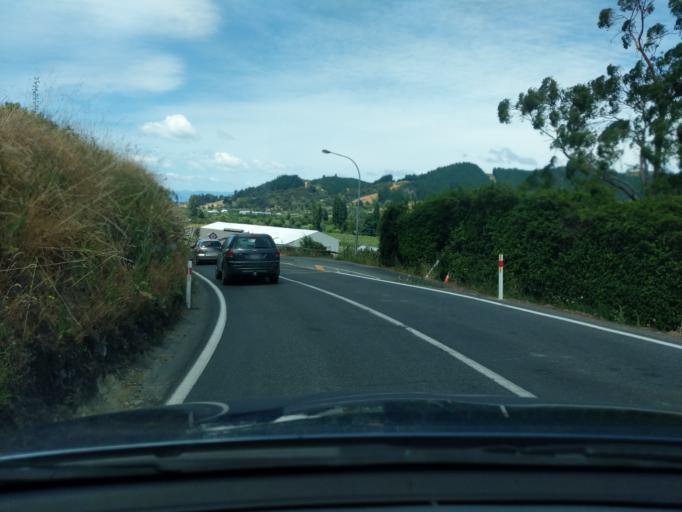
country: NZ
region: Tasman
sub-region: Tasman District
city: Motueka
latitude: -41.0541
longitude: 172.9634
